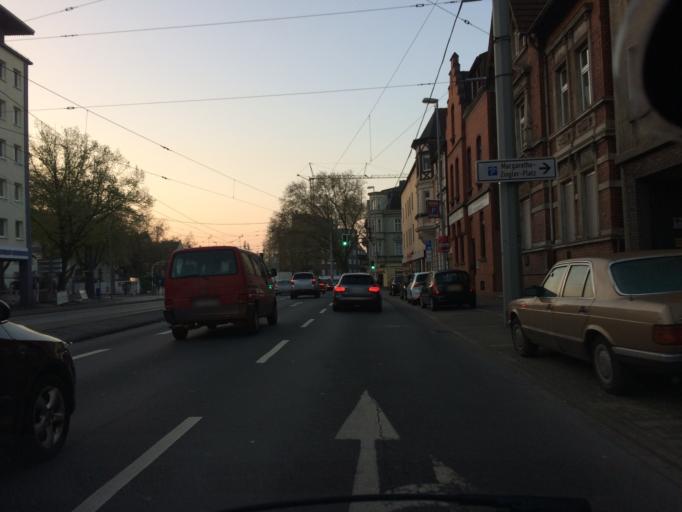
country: DE
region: North Rhine-Westphalia
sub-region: Regierungsbezirk Munster
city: Gelsenkirchen
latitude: 51.5135
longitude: 7.0978
